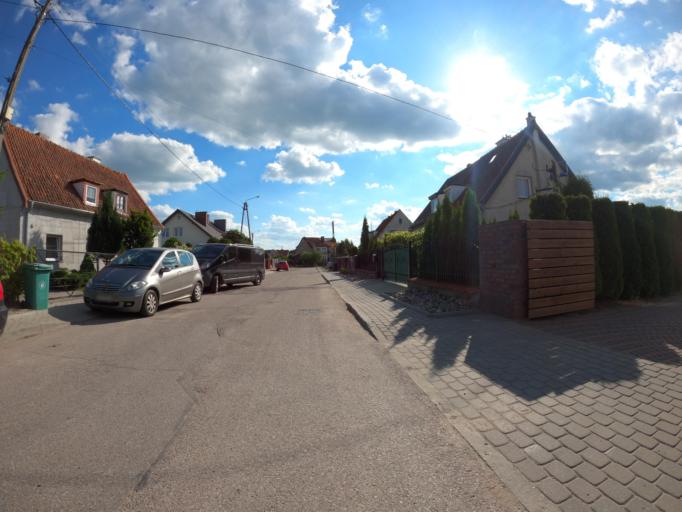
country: PL
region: Warmian-Masurian Voivodeship
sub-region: Powiat lidzbarski
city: Lidzbark Warminski
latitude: 54.1314
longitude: 20.5997
